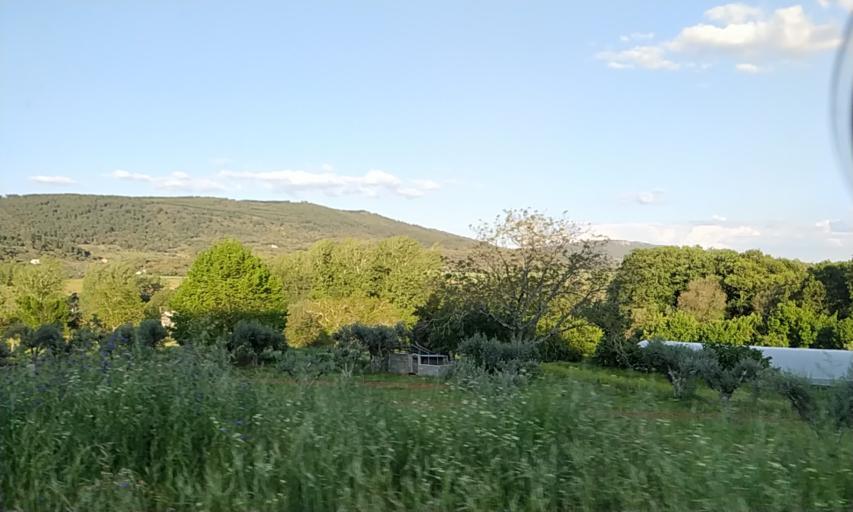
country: PT
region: Portalegre
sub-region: Marvao
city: Marvao
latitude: 39.3677
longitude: -7.3893
